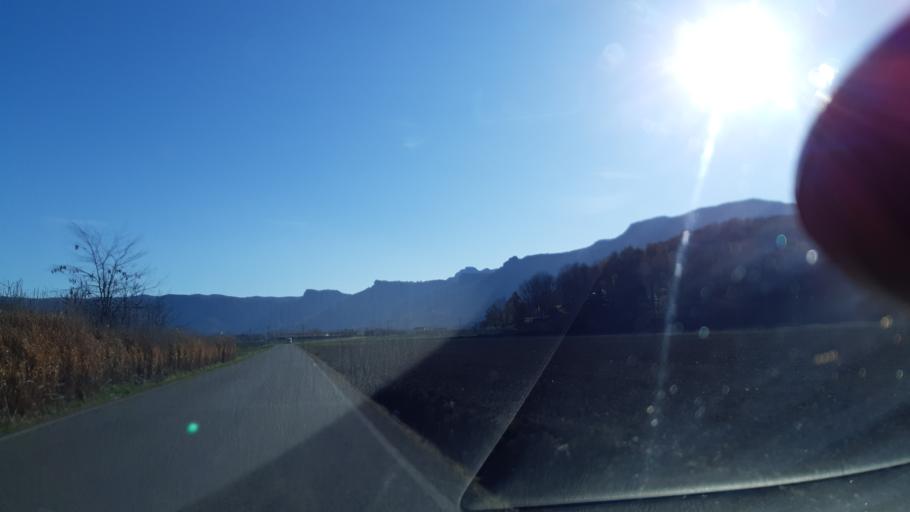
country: ES
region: Catalonia
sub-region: Provincia de Girona
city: Bas
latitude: 42.1411
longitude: 2.4408
